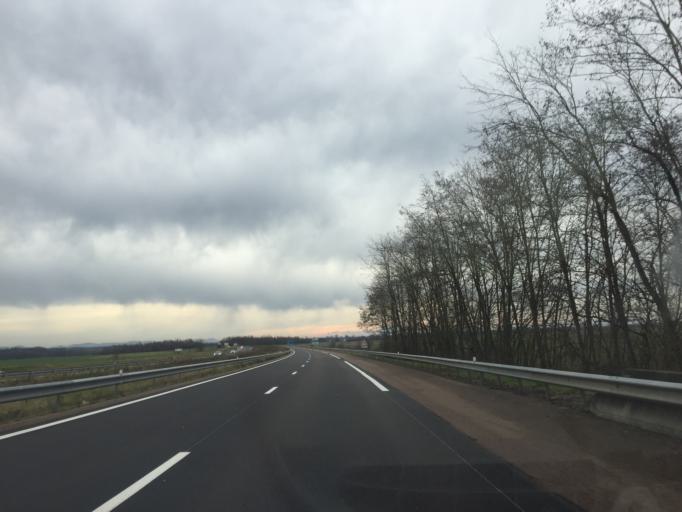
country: FR
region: Franche-Comte
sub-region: Departement du Jura
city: Bletterans
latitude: 46.7690
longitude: 5.5135
